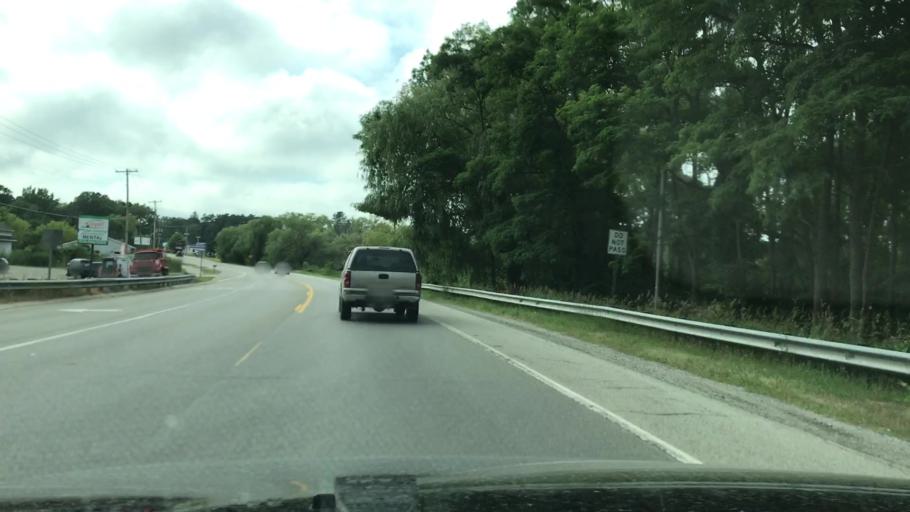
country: US
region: Michigan
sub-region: Ottawa County
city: Spring Lake
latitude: 43.0760
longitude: -86.1684
